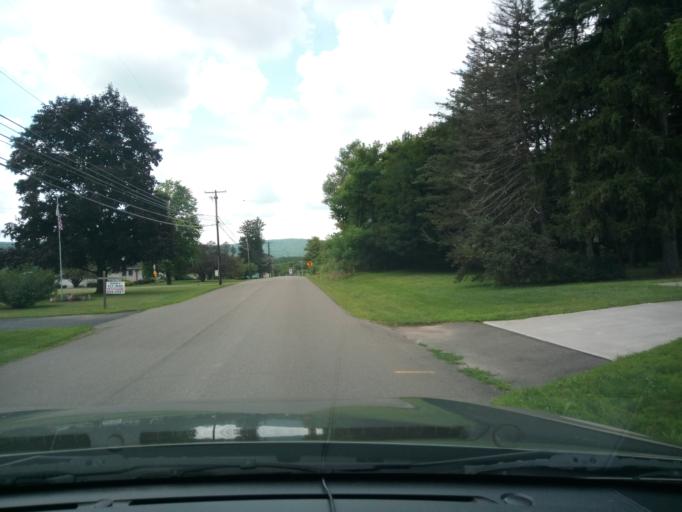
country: US
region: Pennsylvania
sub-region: Bradford County
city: South Waverly
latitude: 41.9836
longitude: -76.5399
